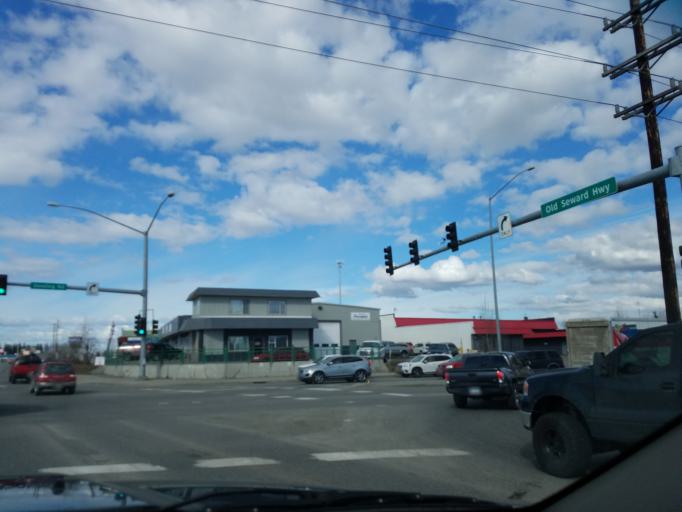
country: US
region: Alaska
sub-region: Anchorage Municipality
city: Anchorage
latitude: 61.1667
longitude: -149.8678
